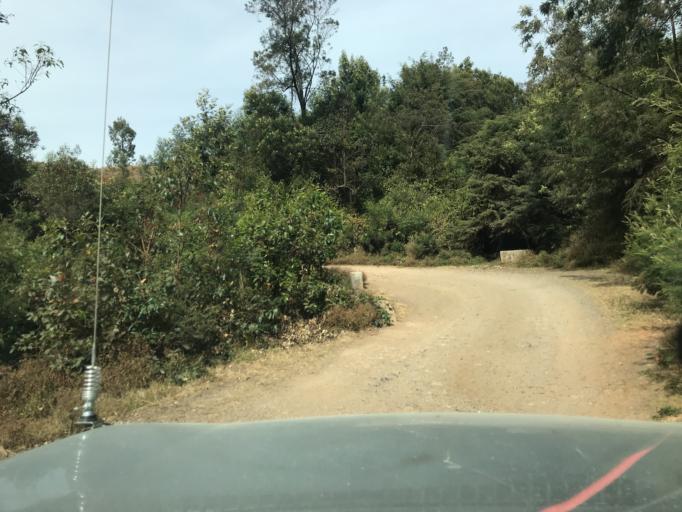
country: TL
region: Ainaro
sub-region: Ainaro
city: Ainaro
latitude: -8.8824
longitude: 125.5388
